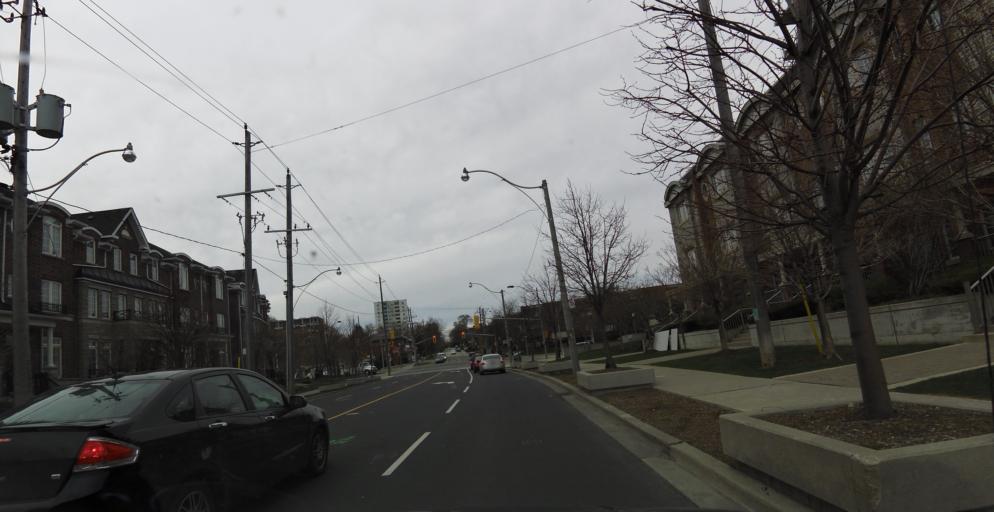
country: CA
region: Ontario
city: Toronto
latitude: 43.6365
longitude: -79.4693
